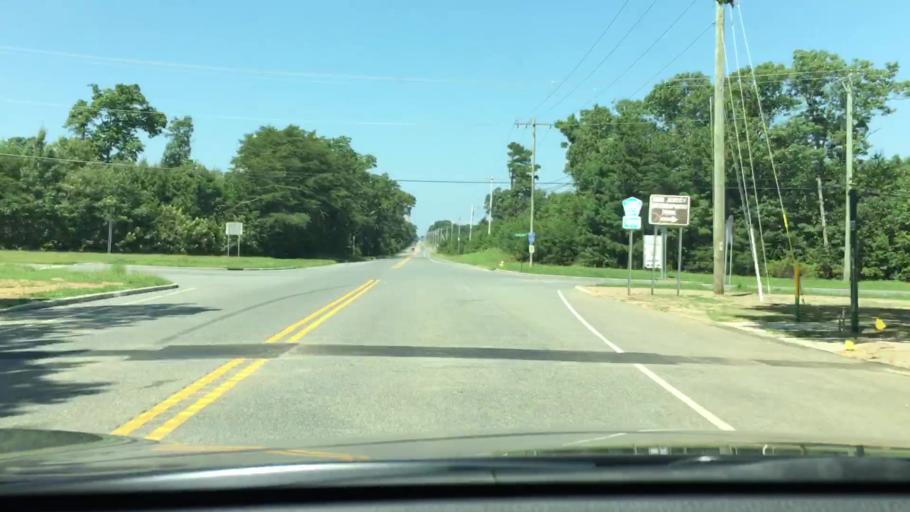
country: US
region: New Jersey
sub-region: Cumberland County
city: Laurel Lake
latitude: 39.3527
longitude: -75.0583
